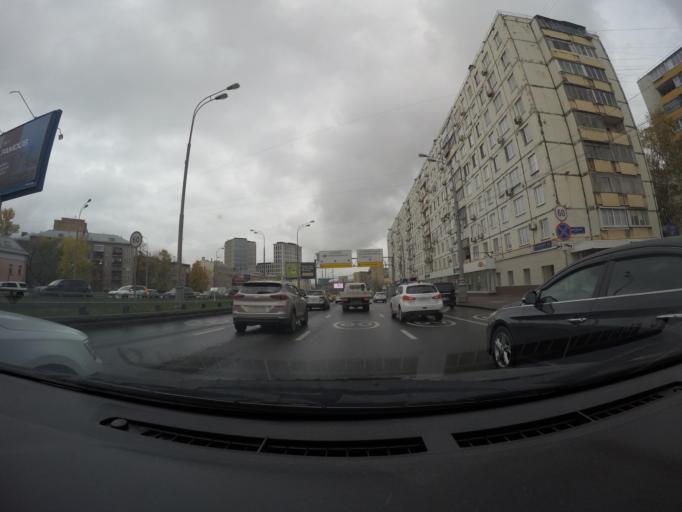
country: RU
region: Moscow
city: Mar'ina Roshcha
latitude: 55.7919
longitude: 37.5772
